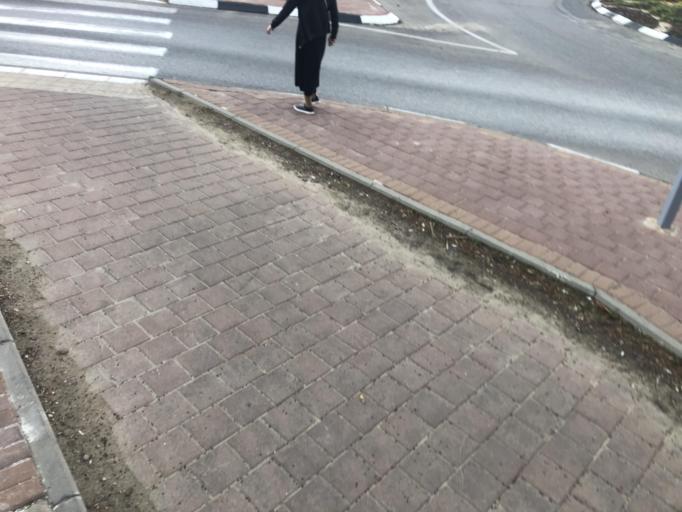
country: IL
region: Jerusalem
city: Modiin Ilit
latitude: 31.9359
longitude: 35.0463
